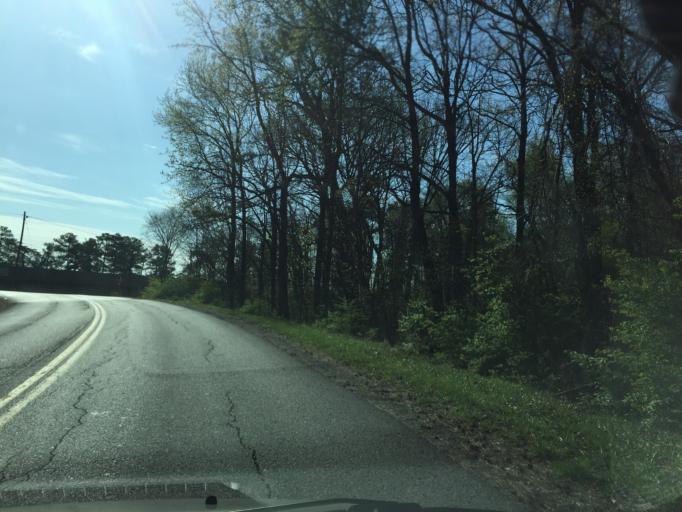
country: US
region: Tennessee
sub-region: Hamilton County
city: East Chattanooga
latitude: 35.0648
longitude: -85.1973
